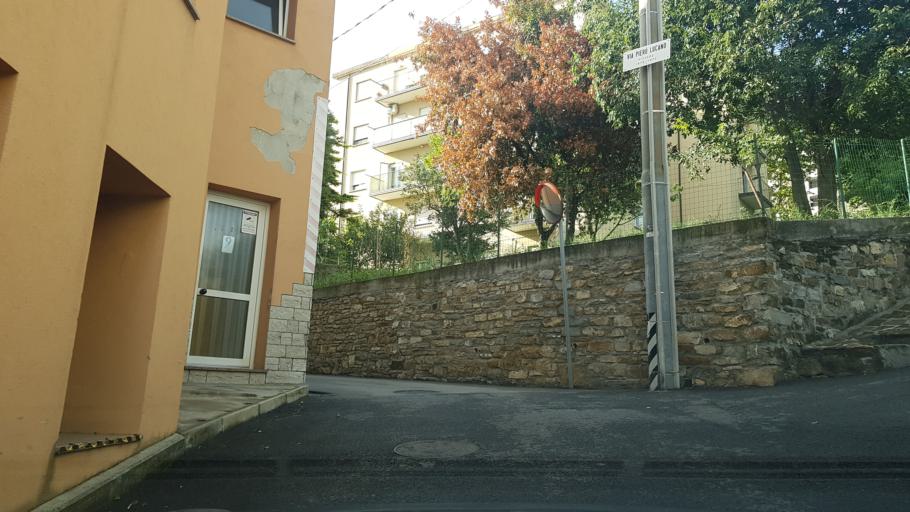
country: IT
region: Friuli Venezia Giulia
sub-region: Provincia di Trieste
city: Trieste
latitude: 45.6412
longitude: 13.8044
